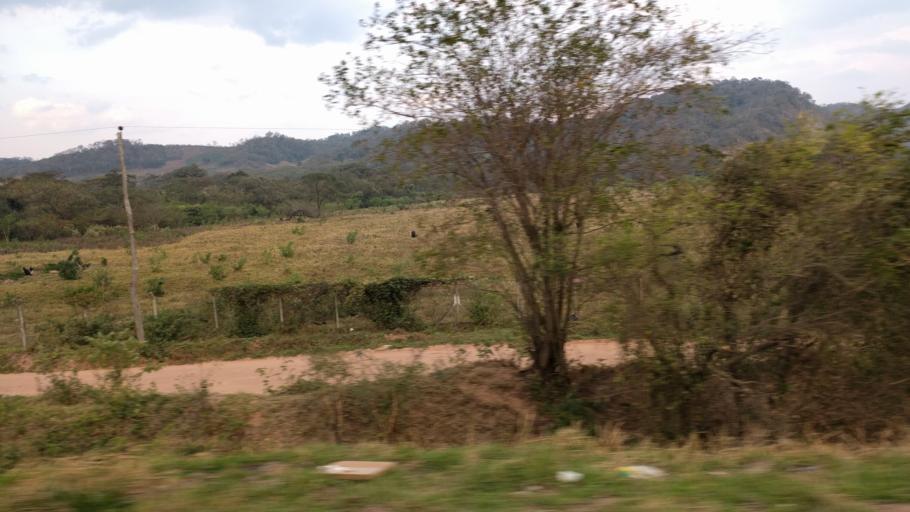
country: BO
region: Santa Cruz
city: Jorochito
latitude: -18.1068
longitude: -63.4570
